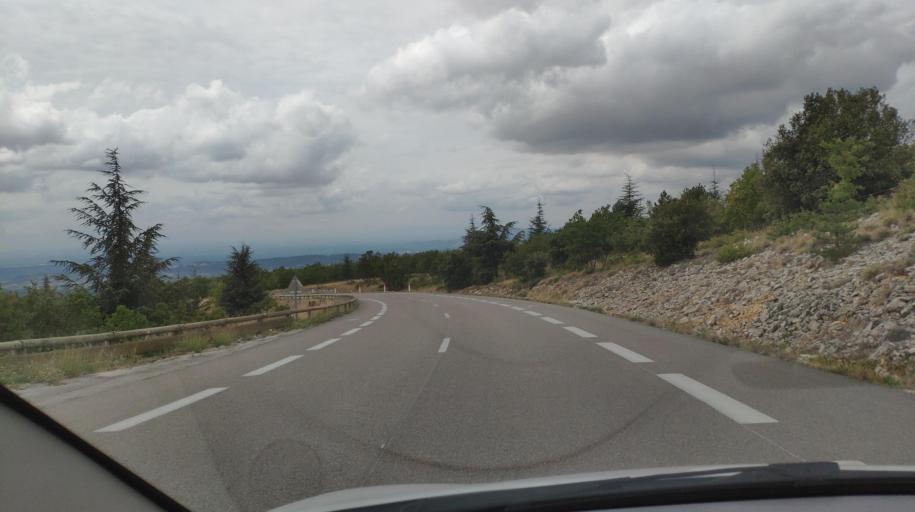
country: FR
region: Provence-Alpes-Cote d'Azur
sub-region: Departement du Vaucluse
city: Villes-sur-Auzon
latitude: 44.0836
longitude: 5.2772
